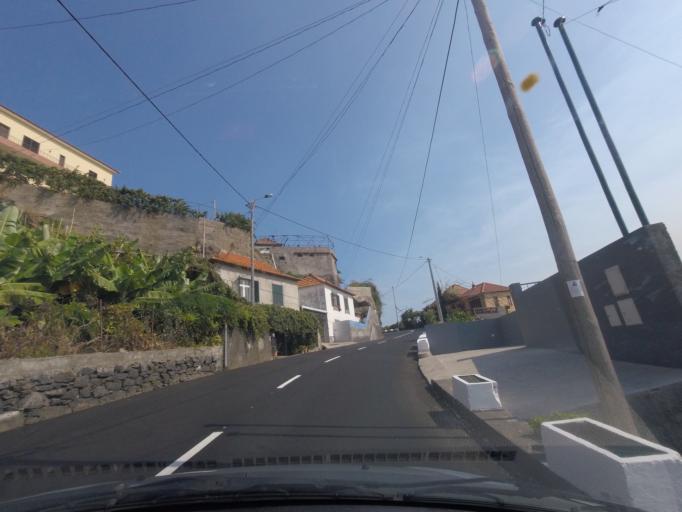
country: PT
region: Madeira
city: Ribeira Brava
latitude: 32.6713
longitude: -17.0607
